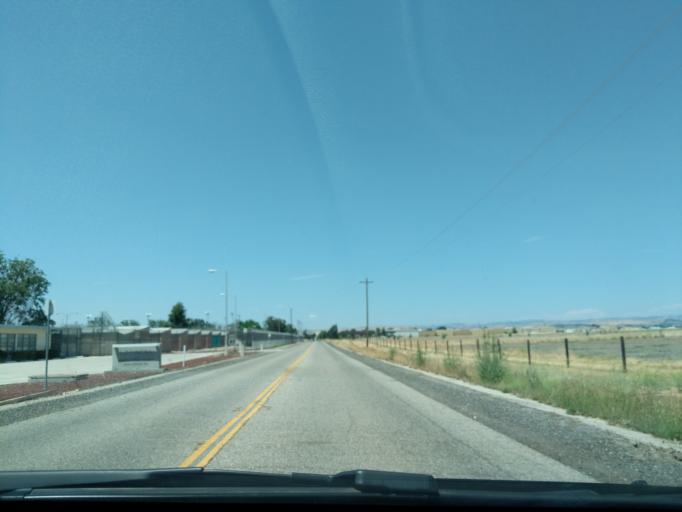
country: US
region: California
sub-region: San Luis Obispo County
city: Paso Robles
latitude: 35.6643
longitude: -120.6410
